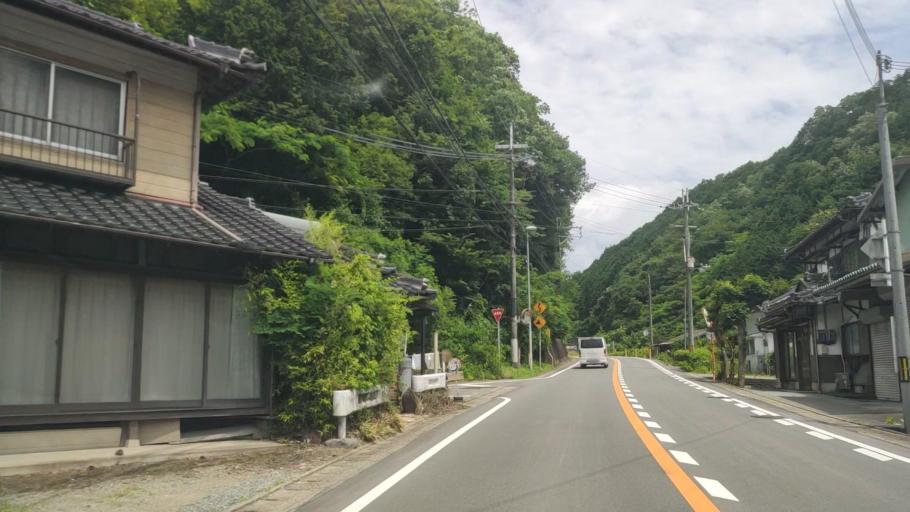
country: JP
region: Hyogo
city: Yamazakicho-nakabirose
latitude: 34.9928
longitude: 134.3994
